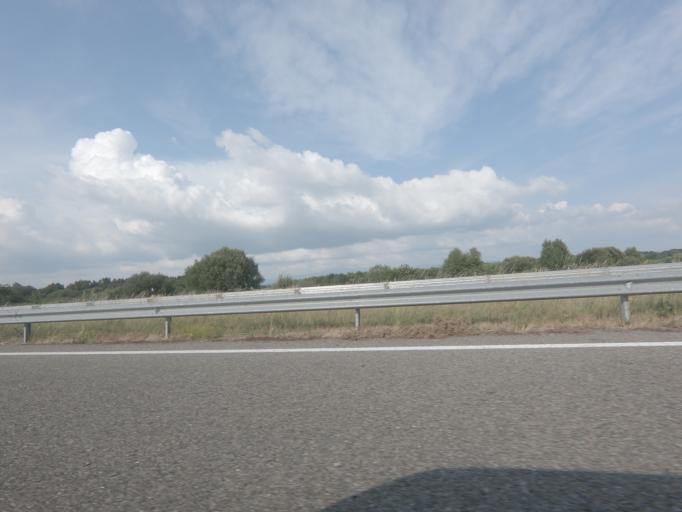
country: ES
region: Galicia
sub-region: Provincia de Ourense
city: Xinzo de Limia
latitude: 42.1138
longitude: -7.7372
